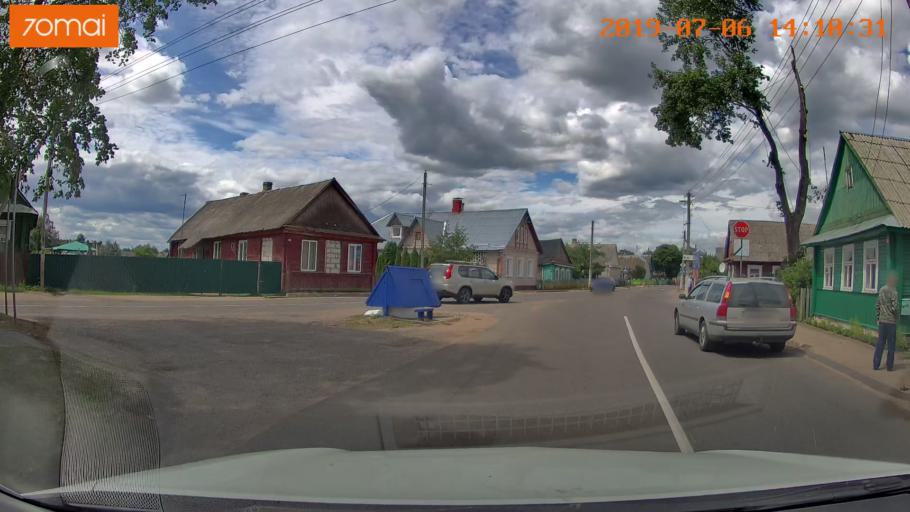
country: BY
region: Minsk
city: Ivyanyets
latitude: 53.8860
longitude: 26.7434
